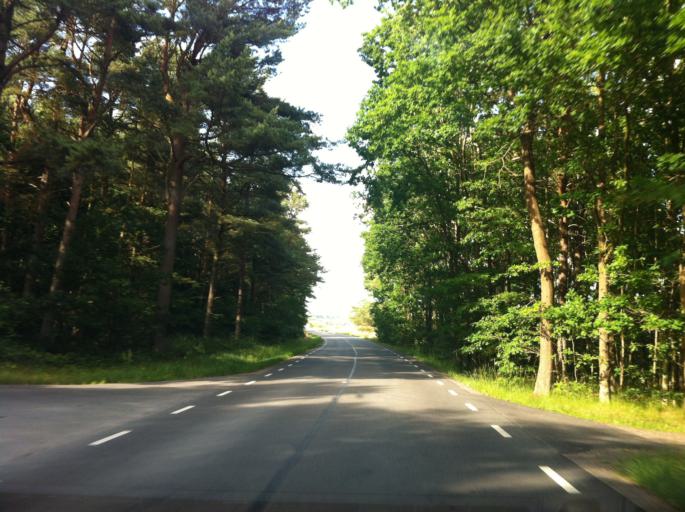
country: SE
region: Skane
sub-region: Simrishamns Kommun
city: Simrishamn
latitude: 55.4541
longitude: 14.2674
